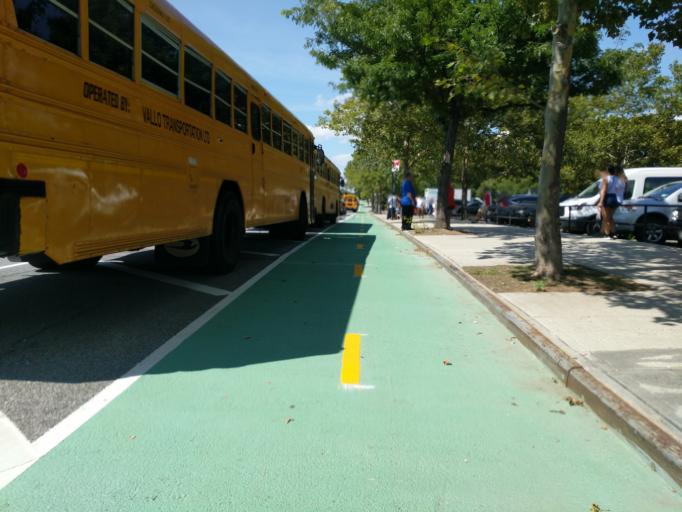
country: US
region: New York
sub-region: Queens County
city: Borough of Queens
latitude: 40.7421
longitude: -73.8507
